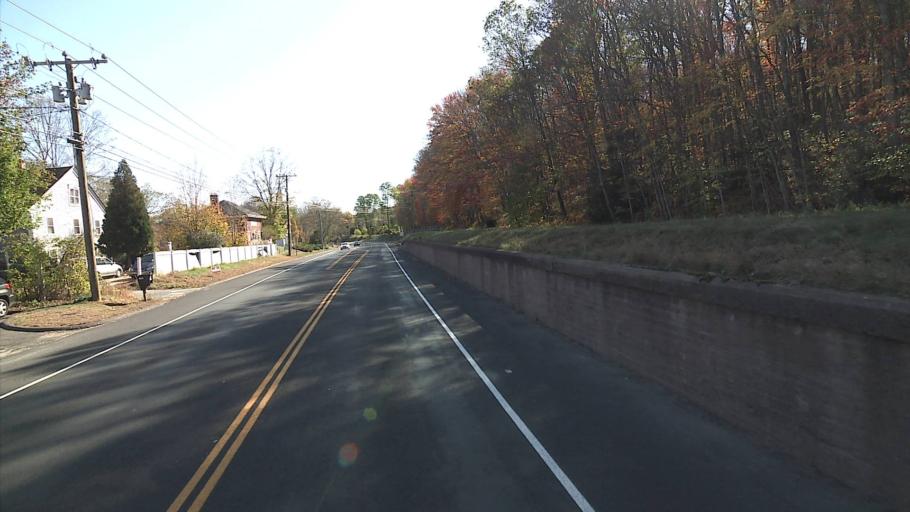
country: US
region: Connecticut
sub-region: Tolland County
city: Coventry Lake
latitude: 41.7397
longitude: -72.3759
